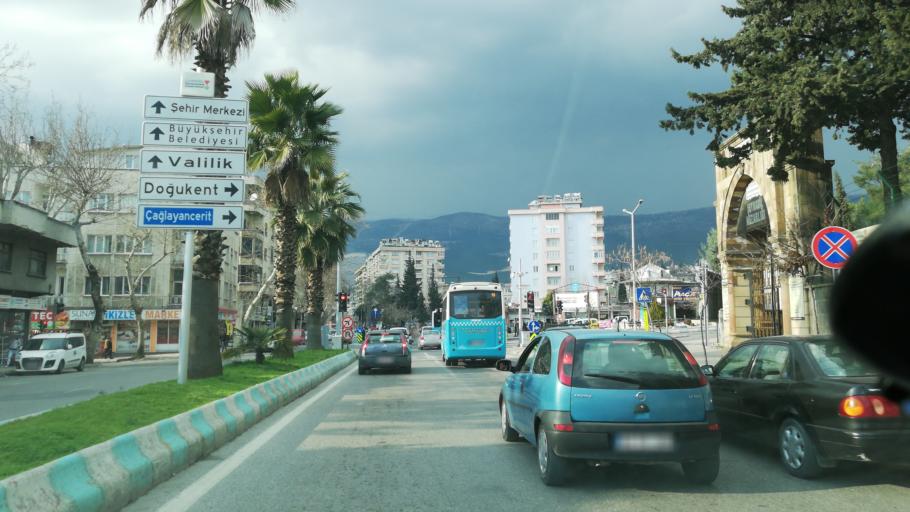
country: TR
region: Kahramanmaras
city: Kahramanmaras
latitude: 37.5774
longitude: 36.9335
